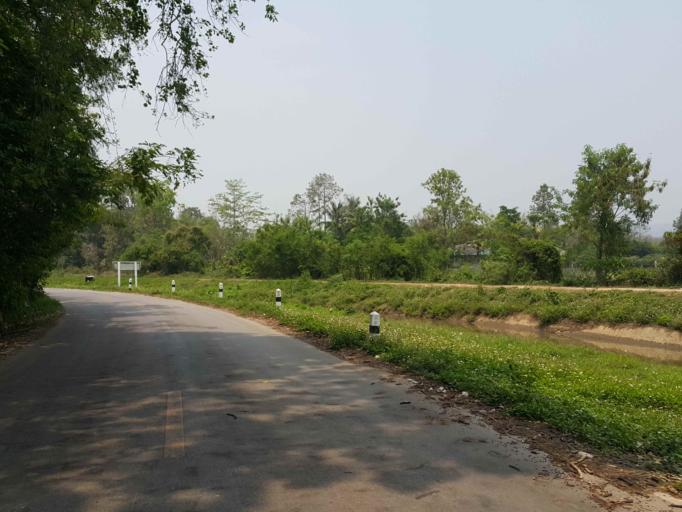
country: TH
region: Chiang Mai
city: San Sai
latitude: 18.8987
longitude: 99.0527
